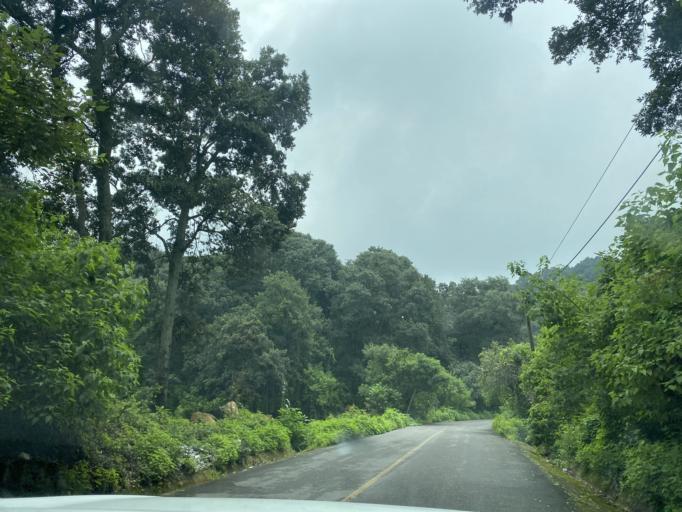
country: MX
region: Morelos
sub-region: Yecapixtla
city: Achichipico
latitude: 18.9393
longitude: -98.8201
